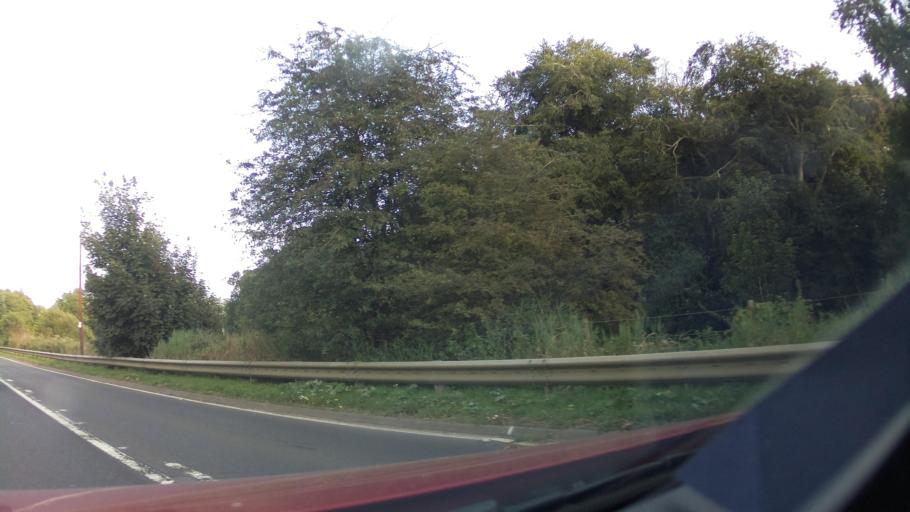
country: GB
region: Scotland
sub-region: Fife
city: Cupar
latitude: 56.3850
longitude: -2.9999
